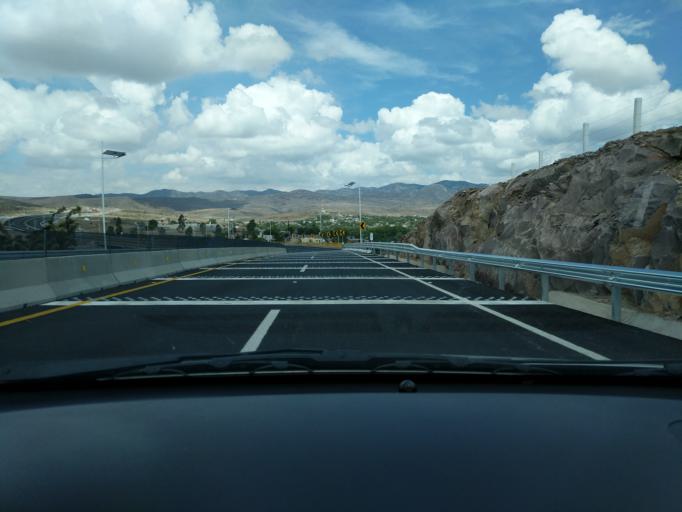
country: MX
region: San Luis Potosi
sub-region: Mexquitic de Carmona
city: Guadalupe Victoria
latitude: 22.1640
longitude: -101.0582
